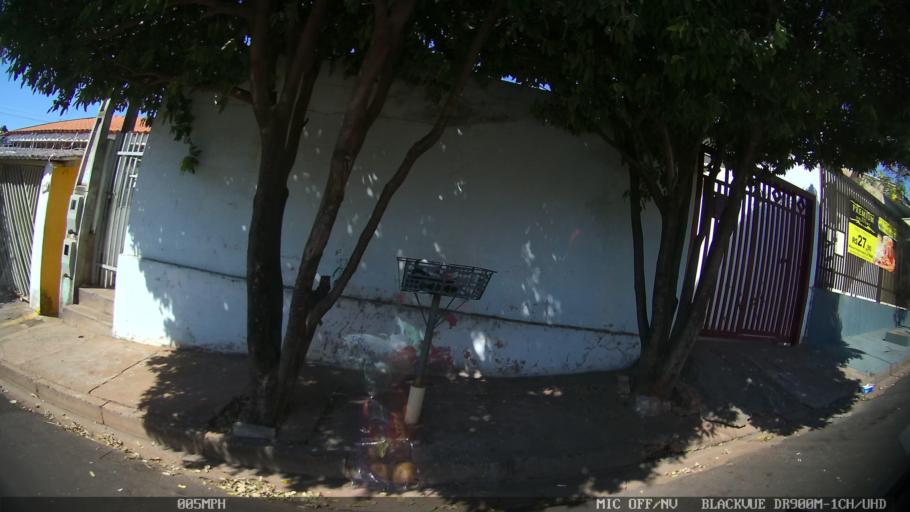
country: BR
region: Sao Paulo
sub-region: Sao Jose Do Rio Preto
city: Sao Jose do Rio Preto
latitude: -20.7744
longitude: -49.4041
